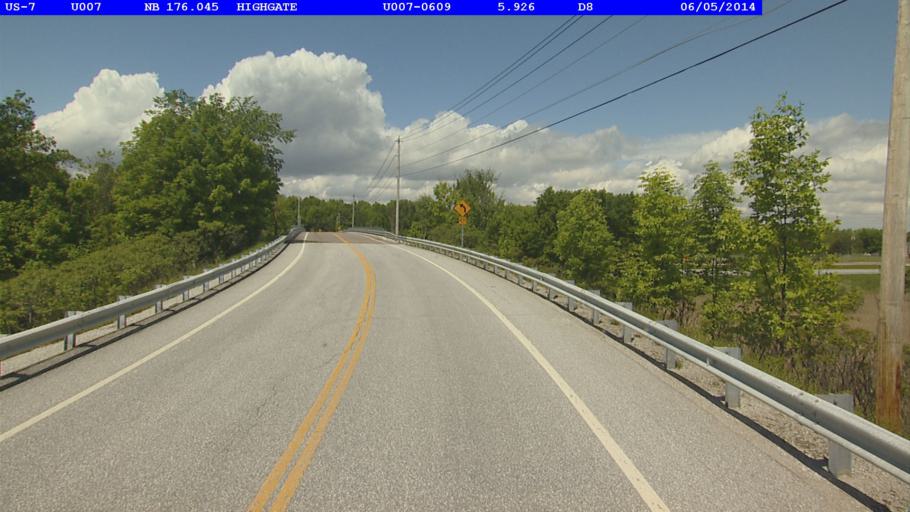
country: US
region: Vermont
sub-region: Franklin County
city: Swanton
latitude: 45.0092
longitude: -73.0845
